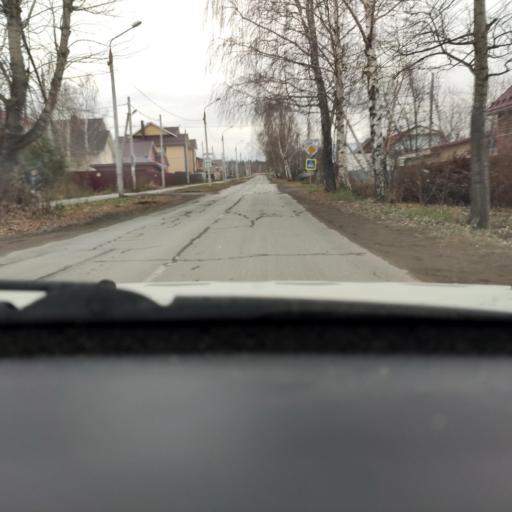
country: RU
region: Perm
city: Polazna
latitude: 58.1274
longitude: 56.3997
